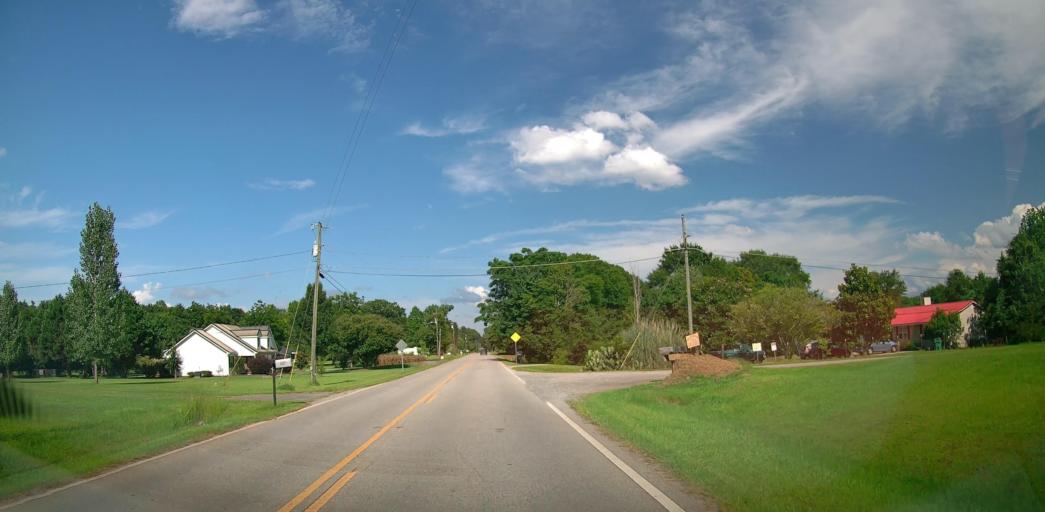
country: US
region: Georgia
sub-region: Houston County
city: Centerville
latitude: 32.5382
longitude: -83.6586
